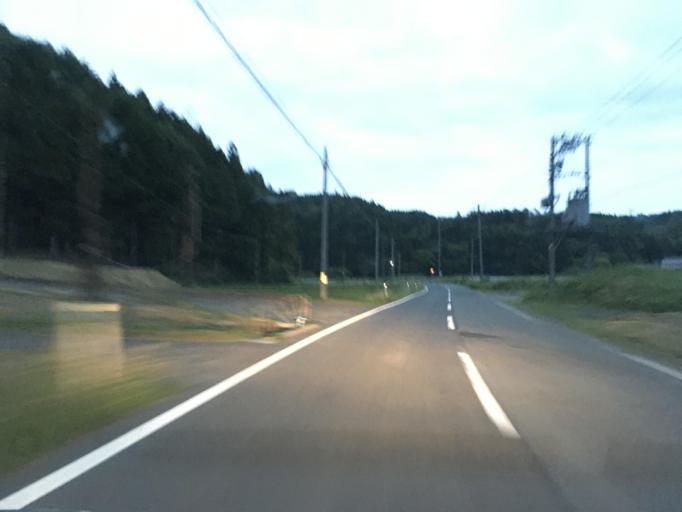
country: JP
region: Miyagi
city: Furukawa
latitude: 38.7651
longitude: 140.8734
